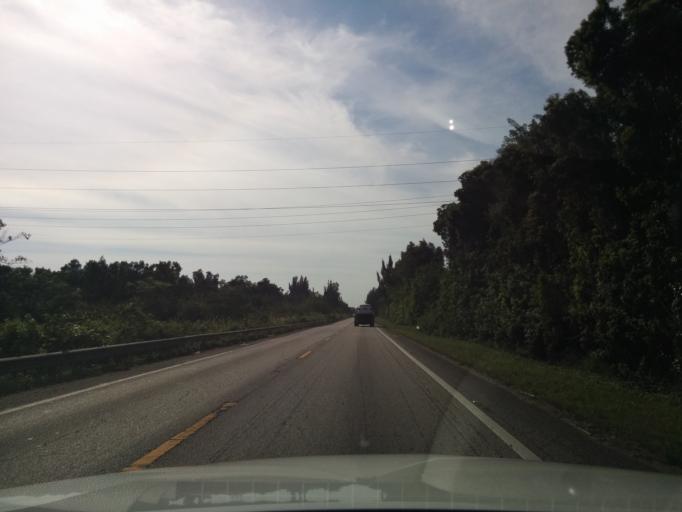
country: US
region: Florida
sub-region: Miami-Dade County
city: Kendall West
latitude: 25.7285
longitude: -80.4801
